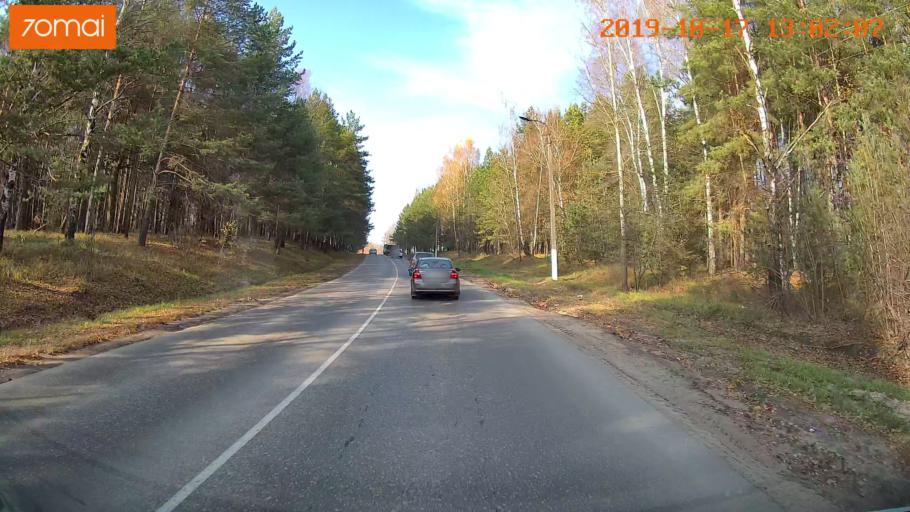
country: RU
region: Rjazan
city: Kasimov
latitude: 54.9483
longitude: 41.3641
